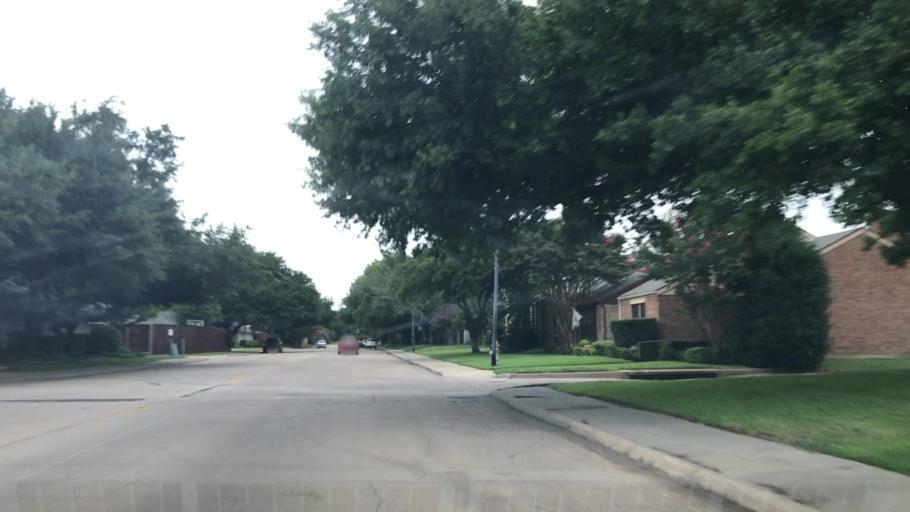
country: US
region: Texas
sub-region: Dallas County
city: Addison
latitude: 32.9653
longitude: -96.7913
